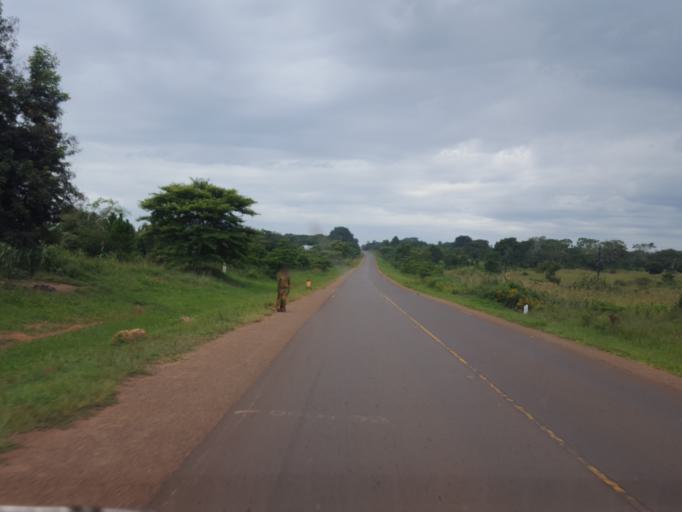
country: UG
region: Central Region
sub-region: Kiboga District
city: Kiboga
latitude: 1.0406
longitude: 31.6713
